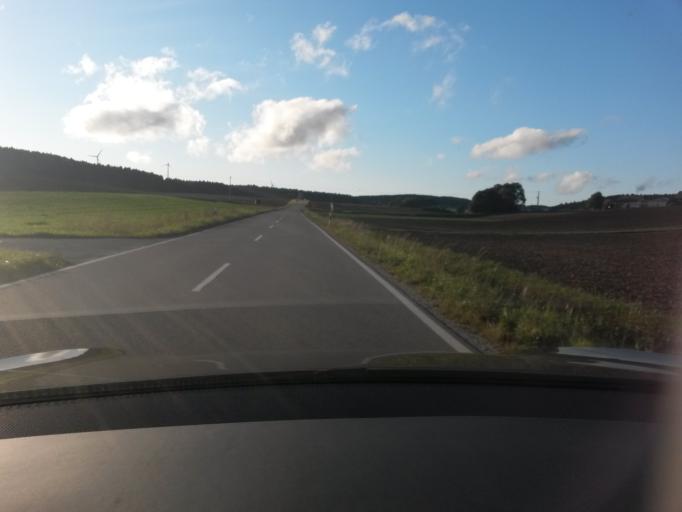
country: DE
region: Bavaria
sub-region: Upper Palatinate
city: Hohenfels
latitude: 49.1559
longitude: 11.8385
